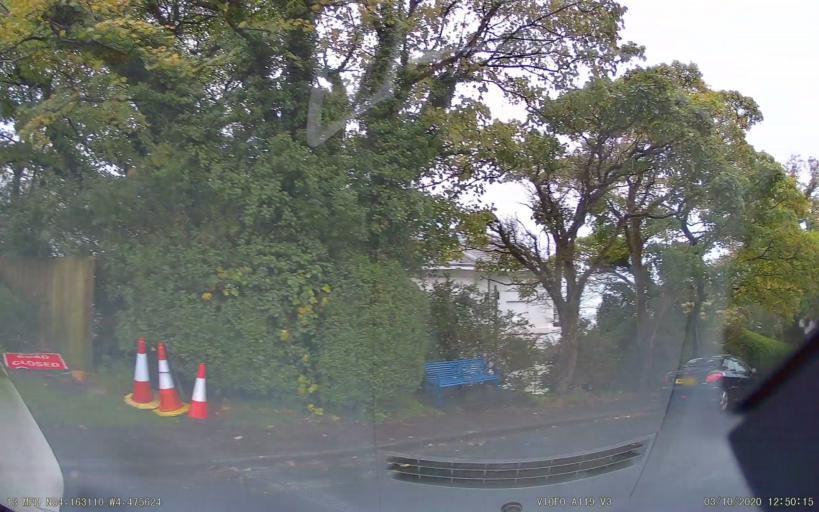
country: IM
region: Douglas
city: Douglas
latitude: 54.1631
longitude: -4.4756
